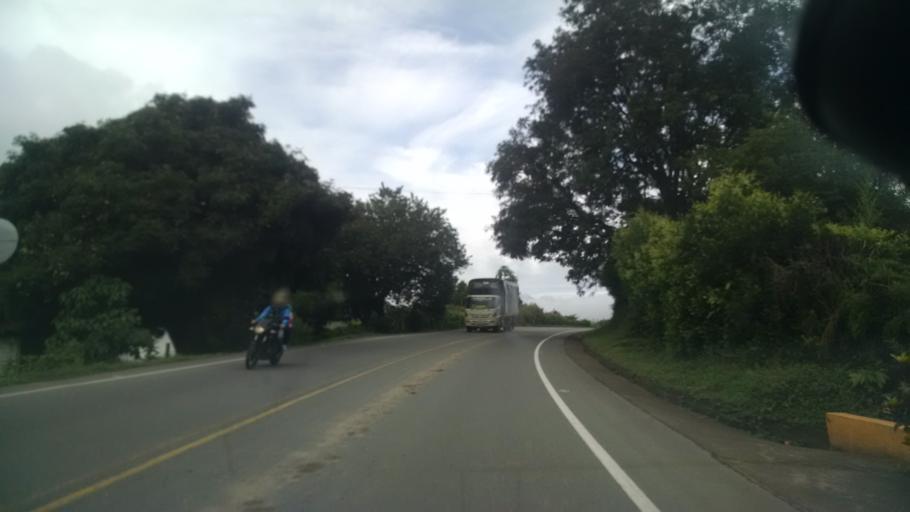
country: CO
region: Caldas
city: Palestina
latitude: 5.0688
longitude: -75.6379
